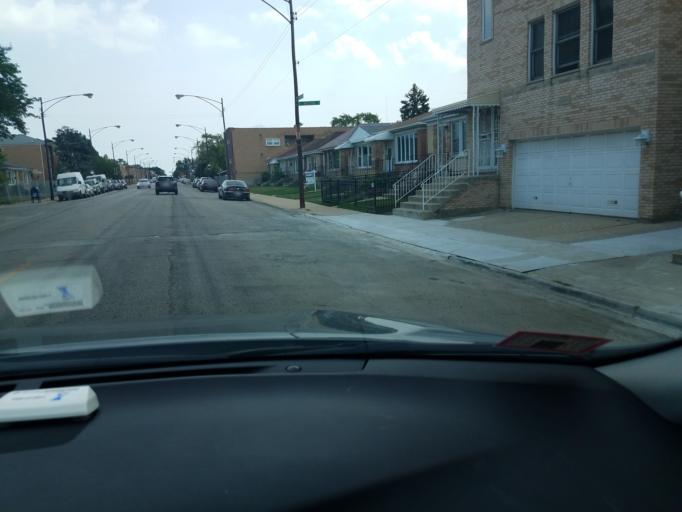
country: US
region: Illinois
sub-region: Cook County
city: Niles
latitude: 41.9918
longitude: -87.7815
